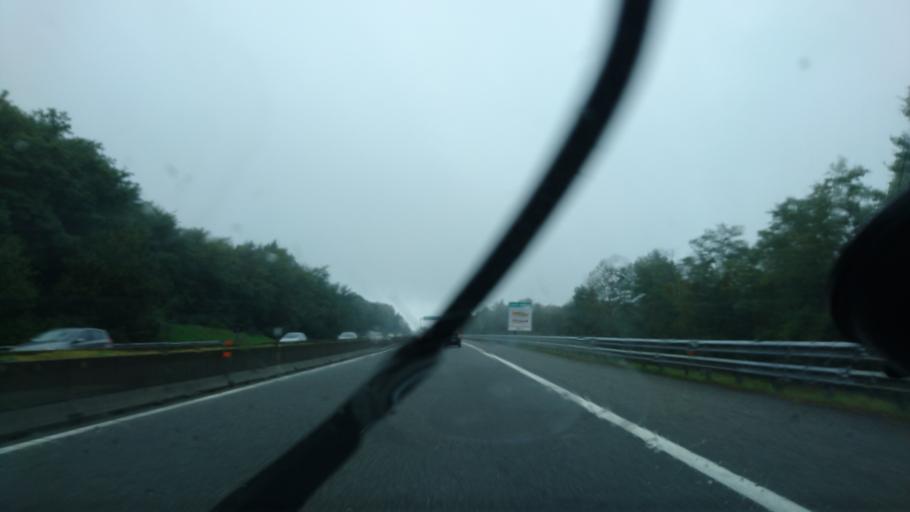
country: IT
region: Piedmont
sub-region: Provincia di Novara
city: Gattico
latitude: 45.7262
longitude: 8.5186
